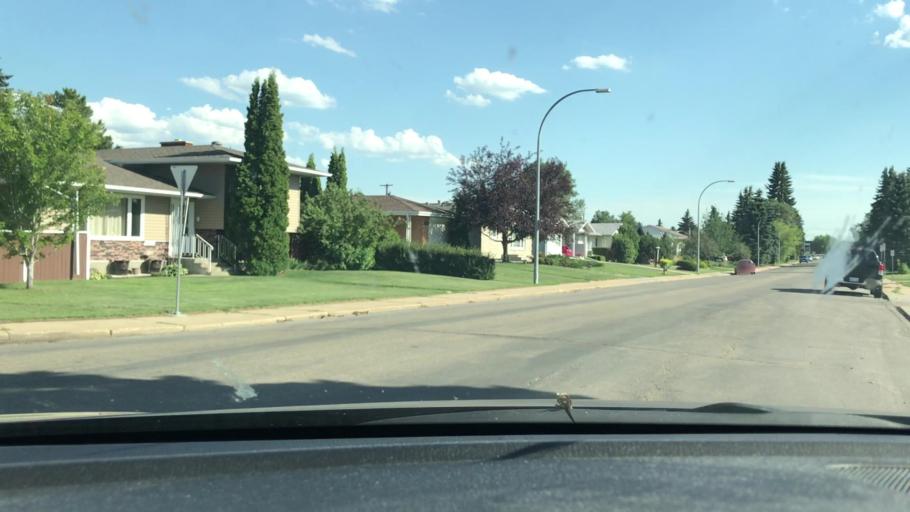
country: CA
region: Alberta
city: Edmonton
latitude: 53.5219
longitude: -113.4229
